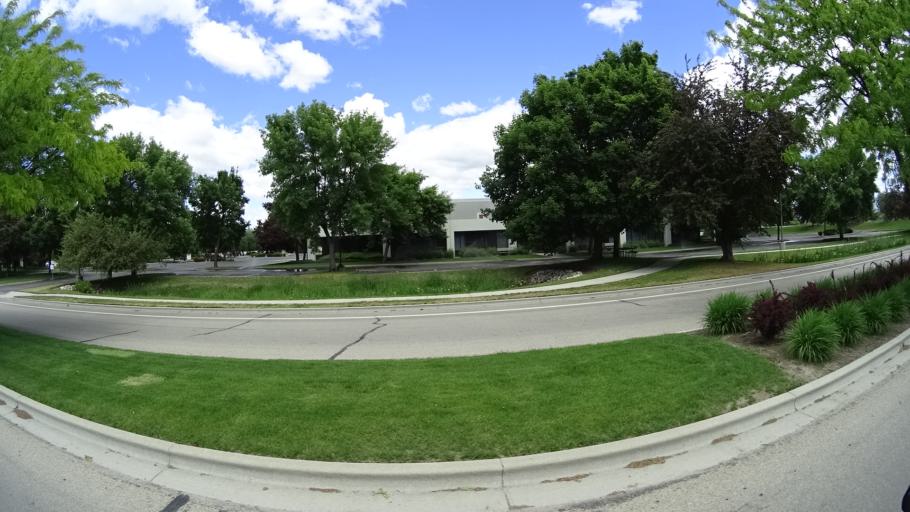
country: US
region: Idaho
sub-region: Ada County
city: Eagle
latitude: 43.6594
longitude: -116.3358
